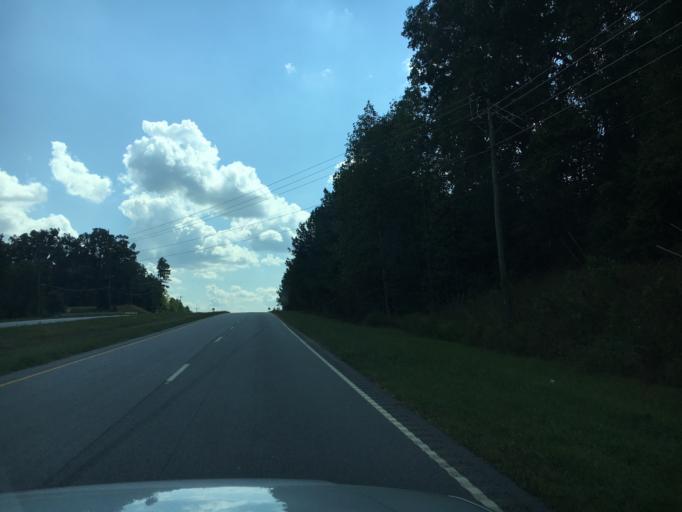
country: US
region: South Carolina
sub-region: Spartanburg County
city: Woodruff
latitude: 34.7862
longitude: -82.0231
